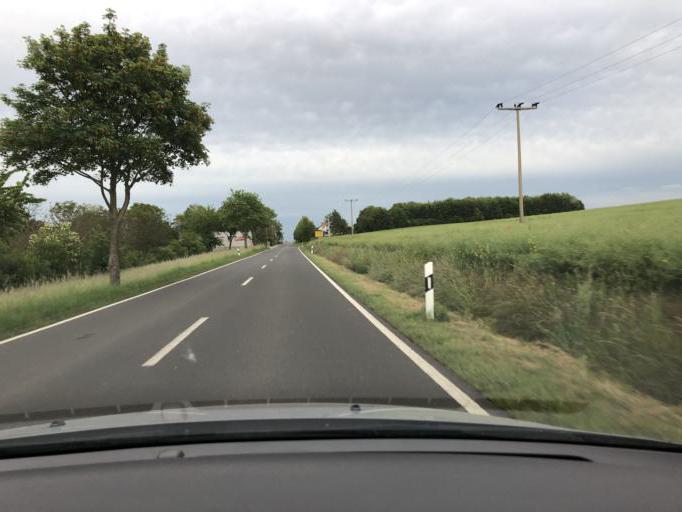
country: DE
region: Thuringia
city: Kodderitzsch
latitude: 51.0956
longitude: 11.4911
